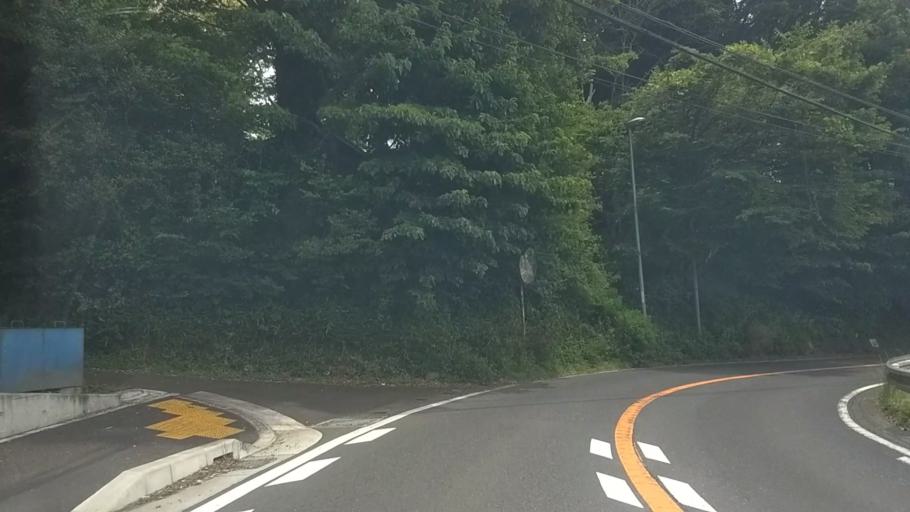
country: JP
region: Kanagawa
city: Chigasaki
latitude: 35.3681
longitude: 139.4220
